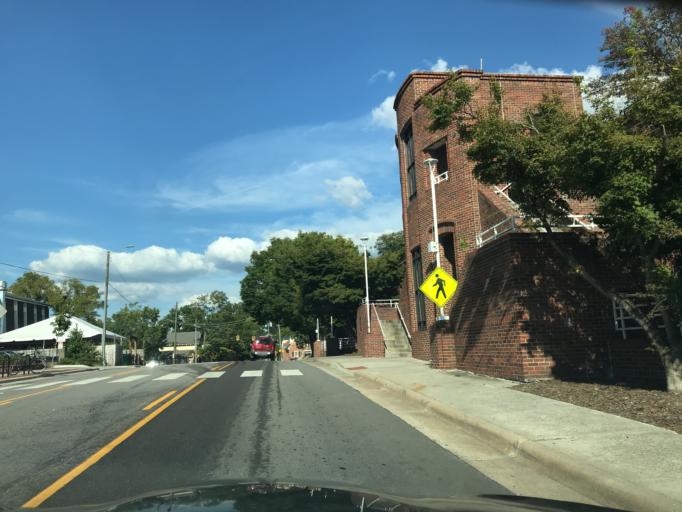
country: US
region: North Carolina
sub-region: Orange County
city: Chapel Hill
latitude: 35.9147
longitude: -79.0546
